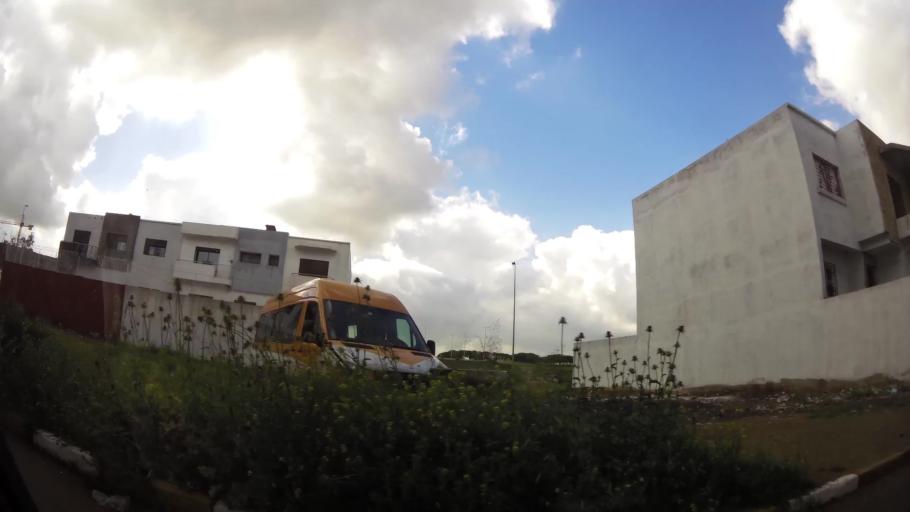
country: MA
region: Grand Casablanca
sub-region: Mediouna
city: Tit Mellil
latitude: 33.5521
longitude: -7.4736
